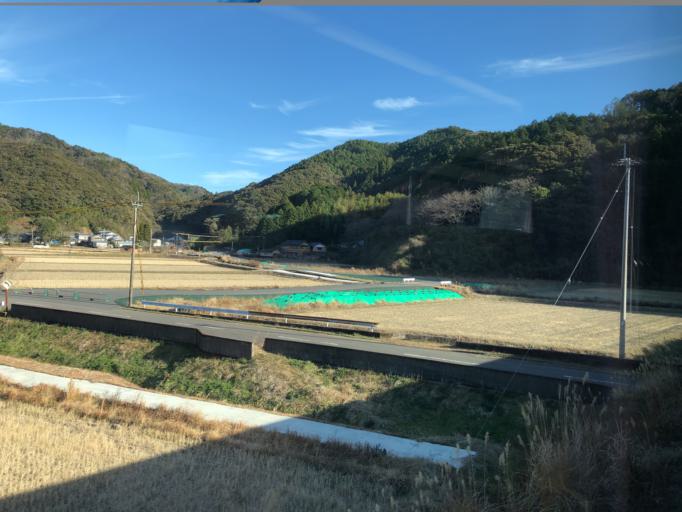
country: JP
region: Kochi
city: Nakamura
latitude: 33.0998
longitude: 133.0996
